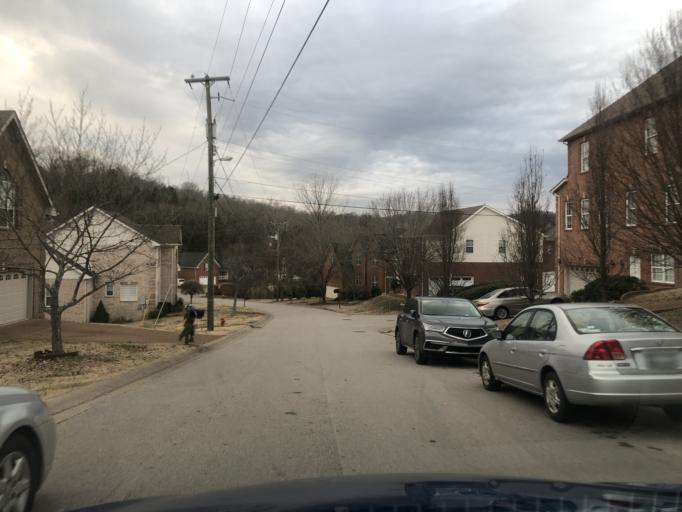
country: US
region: Tennessee
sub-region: Davidson County
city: Belle Meade
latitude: 36.1003
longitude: -86.9282
